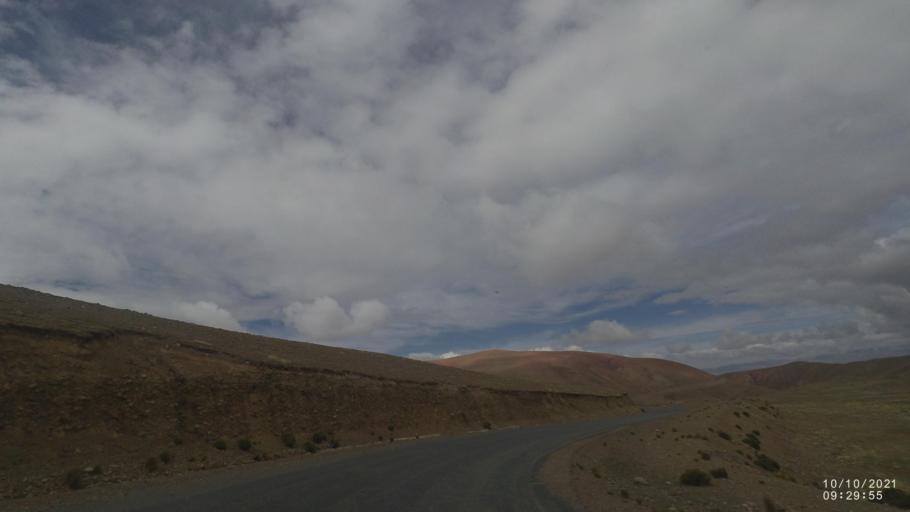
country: BO
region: La Paz
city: Quime
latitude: -17.1178
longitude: -67.3259
